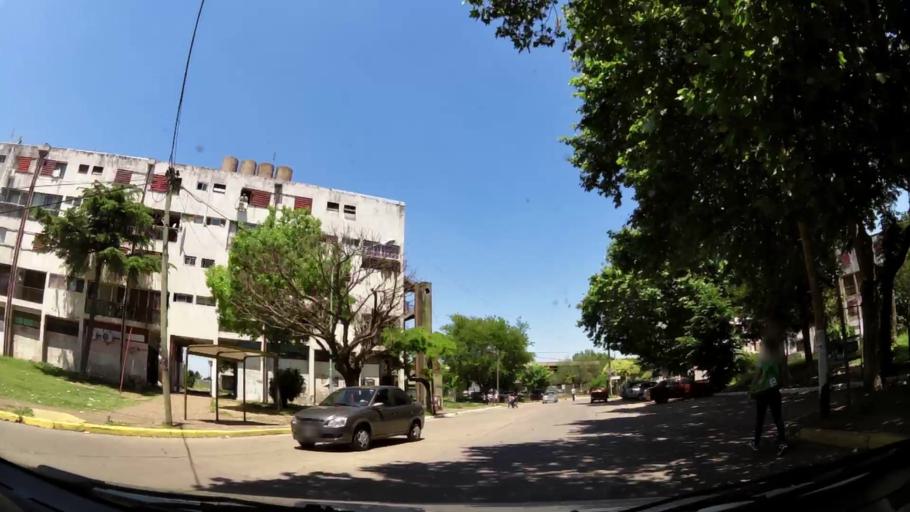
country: AR
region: Buenos Aires
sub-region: Partido de Merlo
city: Merlo
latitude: -34.6526
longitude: -58.7106
